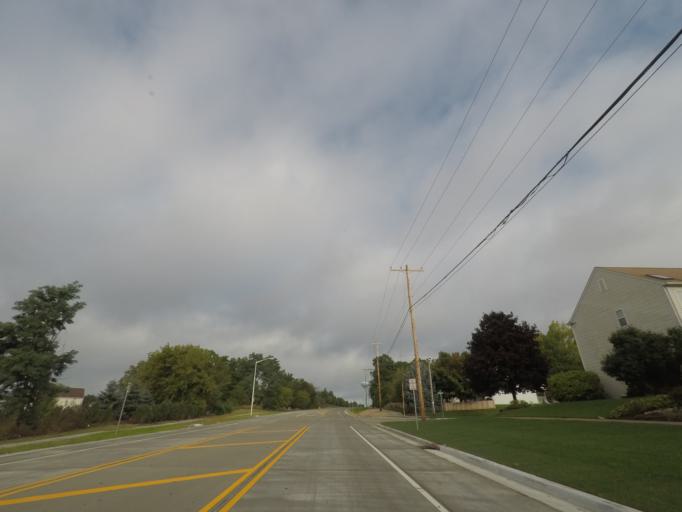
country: US
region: Wisconsin
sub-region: Waukesha County
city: Pewaukee
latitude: 43.0336
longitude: -88.2794
